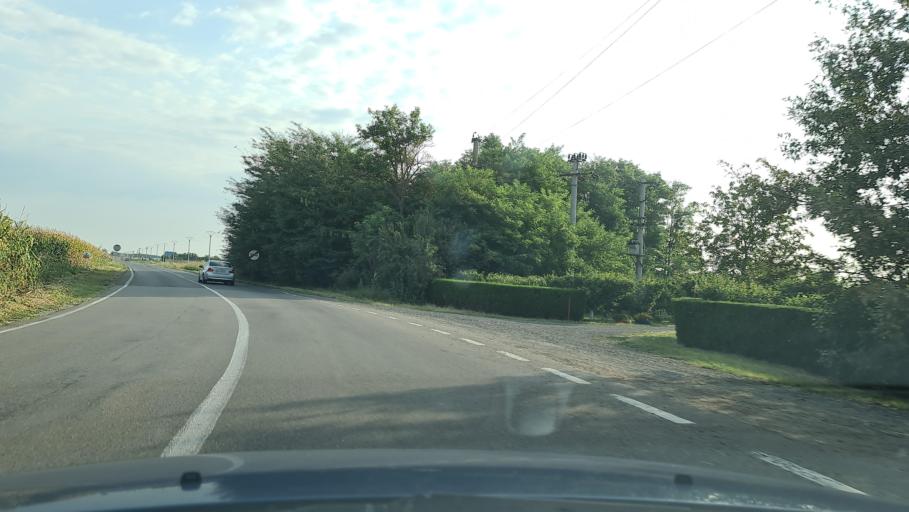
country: RO
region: Calarasi
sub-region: Oras Lehliu Gara
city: Razvani
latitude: 44.4371
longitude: 26.8894
